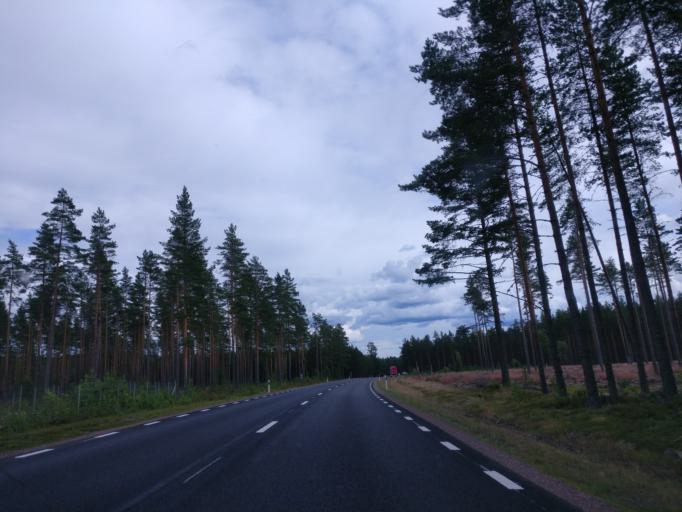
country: SE
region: Vaermland
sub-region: Hagfors Kommun
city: Hagfors
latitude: 60.0459
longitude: 13.5778
